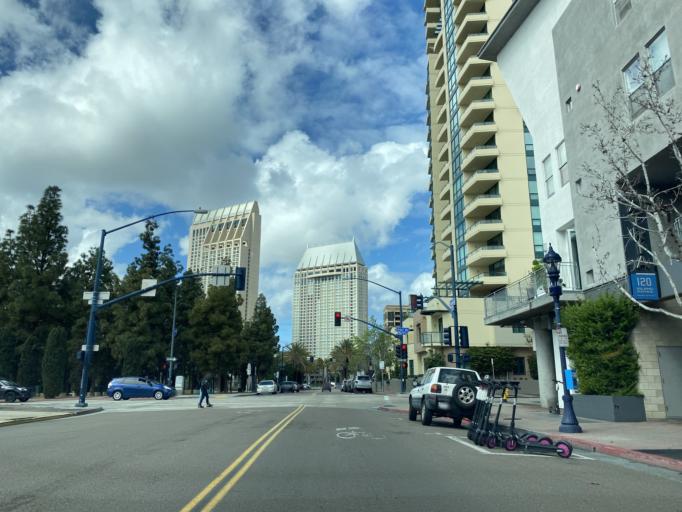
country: US
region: California
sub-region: San Diego County
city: San Diego
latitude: 32.7104
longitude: -117.1633
